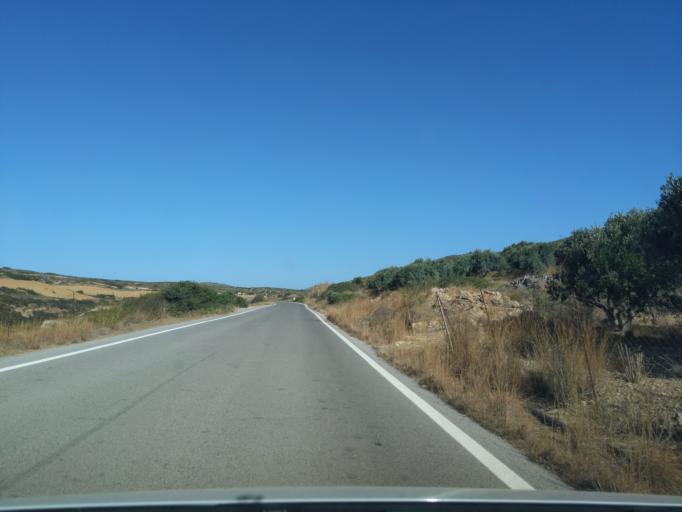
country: GR
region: Crete
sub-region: Nomos Lasithiou
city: Palekastro
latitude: 35.2294
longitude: 26.2545
